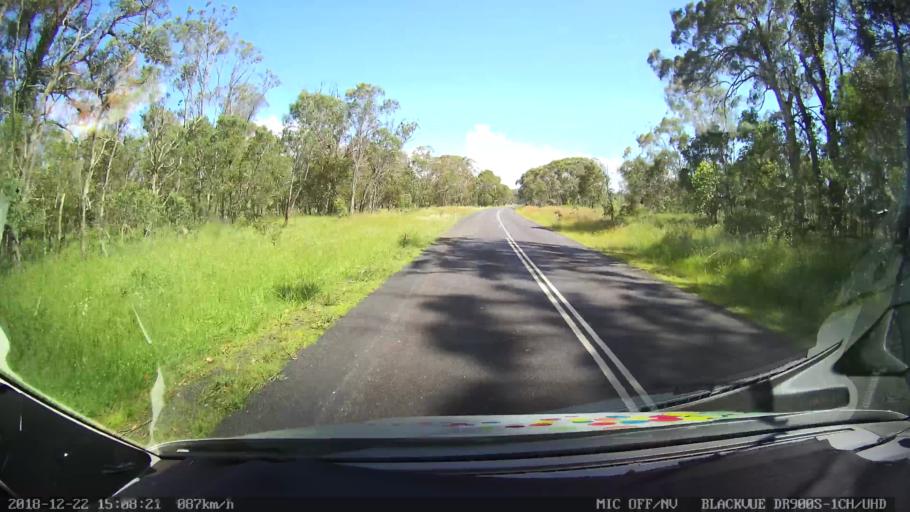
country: AU
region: New South Wales
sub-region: Bellingen
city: Dorrigo
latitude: -30.3112
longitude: 152.4140
